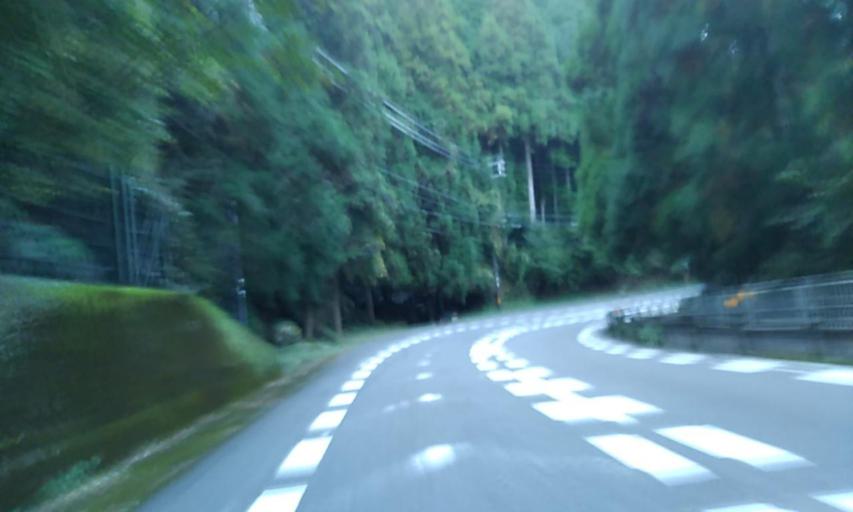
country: JP
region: Wakayama
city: Shingu
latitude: 33.7318
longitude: 135.9443
